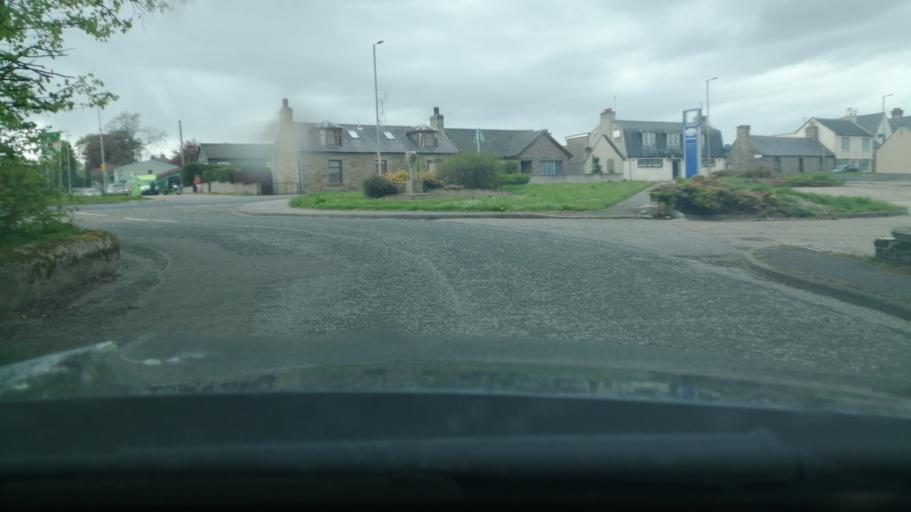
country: GB
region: Scotland
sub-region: Moray
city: Keith
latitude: 57.5359
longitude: -2.9485
